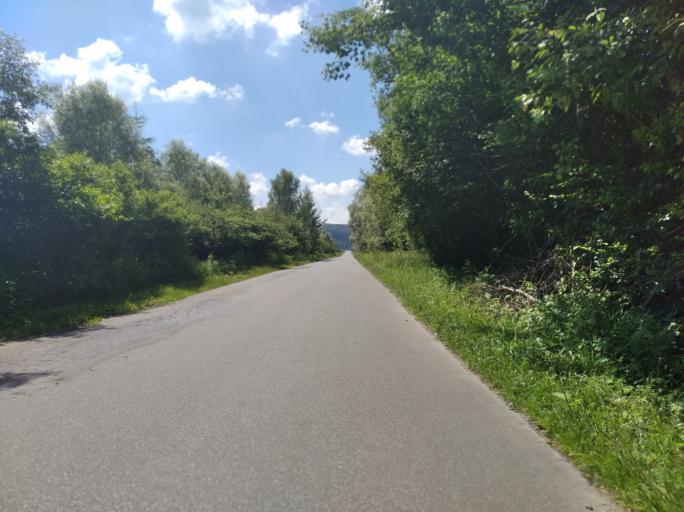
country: PL
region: Subcarpathian Voivodeship
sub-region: Powiat brzozowski
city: Dydnia
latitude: 49.7079
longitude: 22.2096
